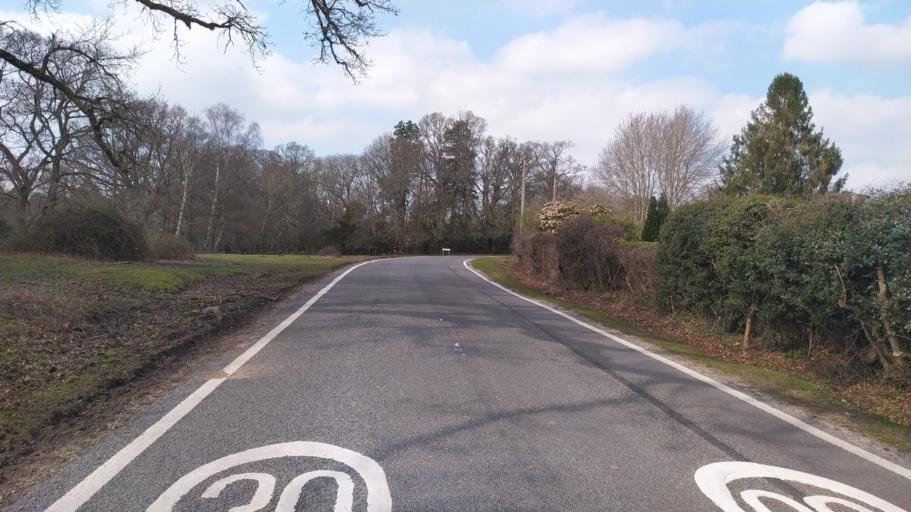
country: GB
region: England
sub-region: Hampshire
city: Cadnam
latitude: 50.9277
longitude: -1.6161
